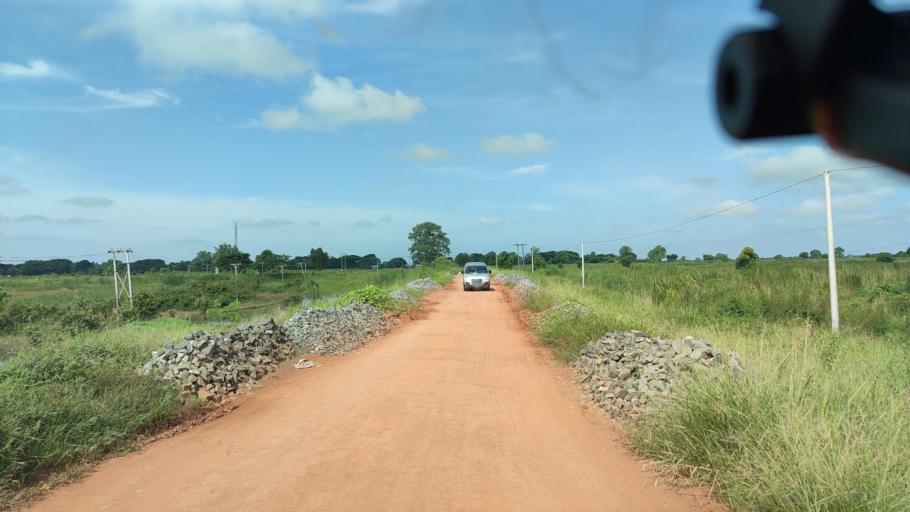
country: MM
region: Bago
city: Letpandan
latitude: 17.7271
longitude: 95.6069
